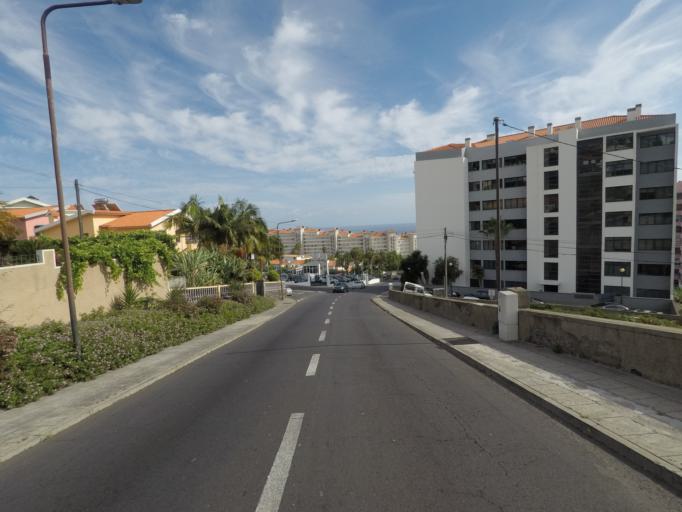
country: PT
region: Madeira
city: Camara de Lobos
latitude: 32.6422
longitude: -16.9444
